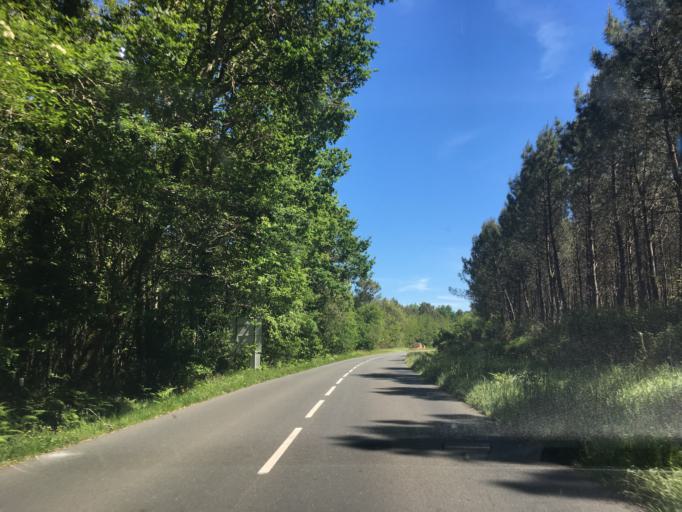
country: FR
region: Aquitaine
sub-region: Departement de la Gironde
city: Lesparre-Medoc
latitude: 45.2845
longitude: -0.8946
